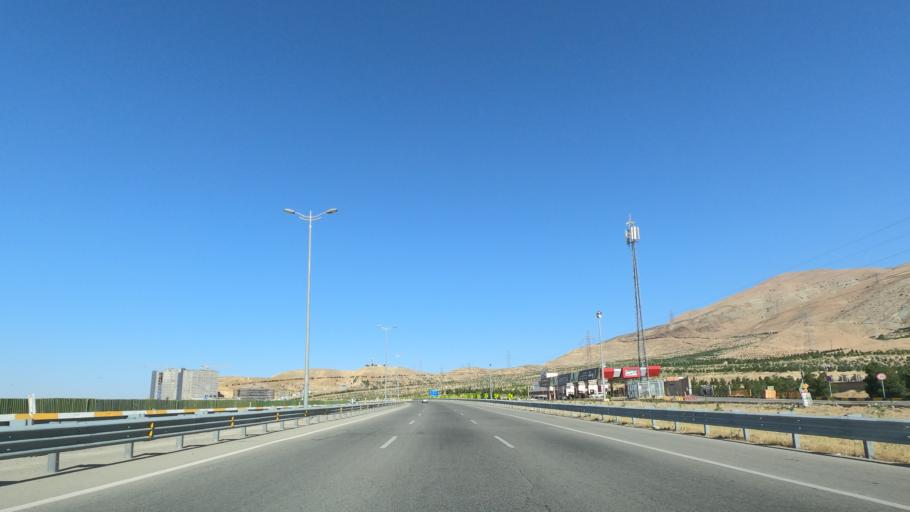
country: IR
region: Tehran
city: Shahr-e Qods
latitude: 35.7525
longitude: 51.1216
